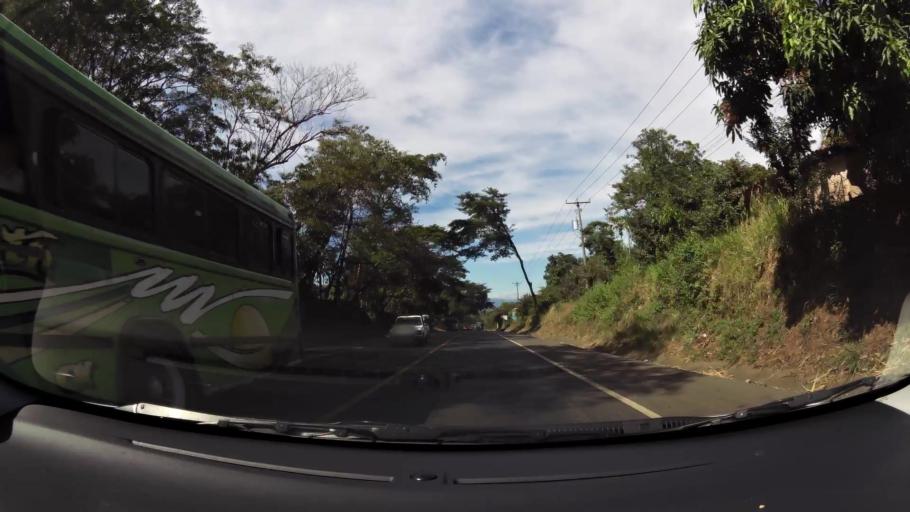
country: SV
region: San Salvador
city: Guazapa
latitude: 13.9159
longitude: -89.1828
